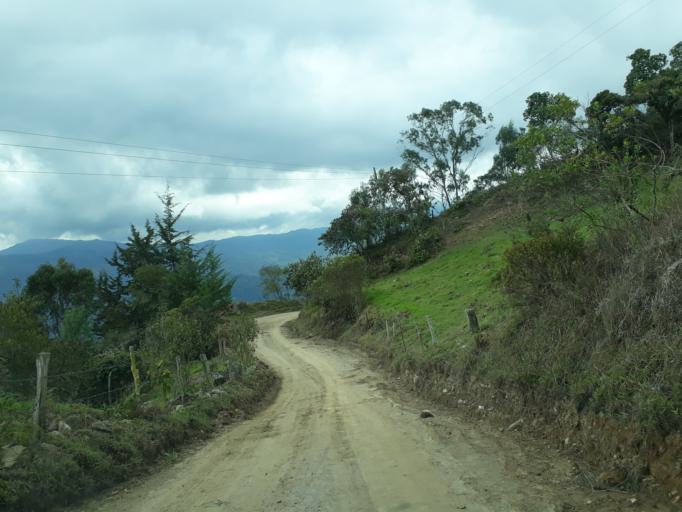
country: CO
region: Cundinamarca
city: Manta
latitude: 5.0199
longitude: -73.5439
